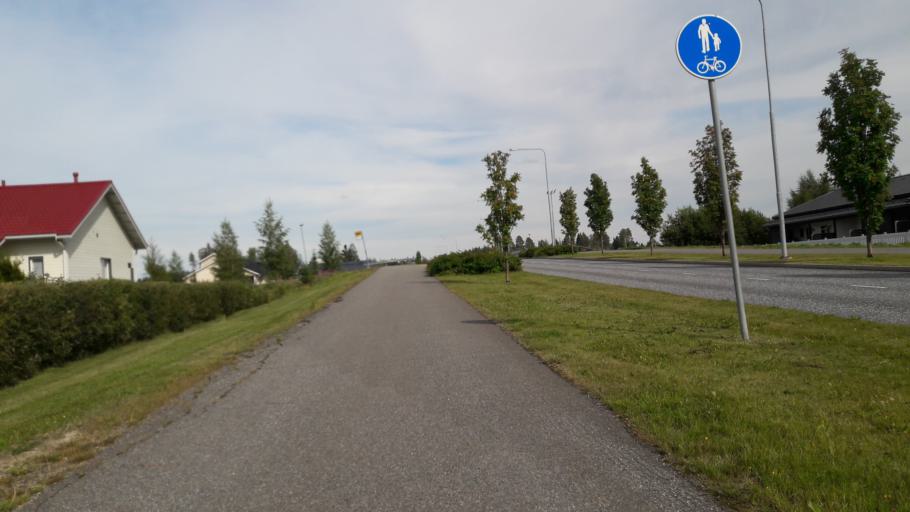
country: FI
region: North Karelia
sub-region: Joensuu
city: Joensuu
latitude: 62.5713
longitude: 29.8110
